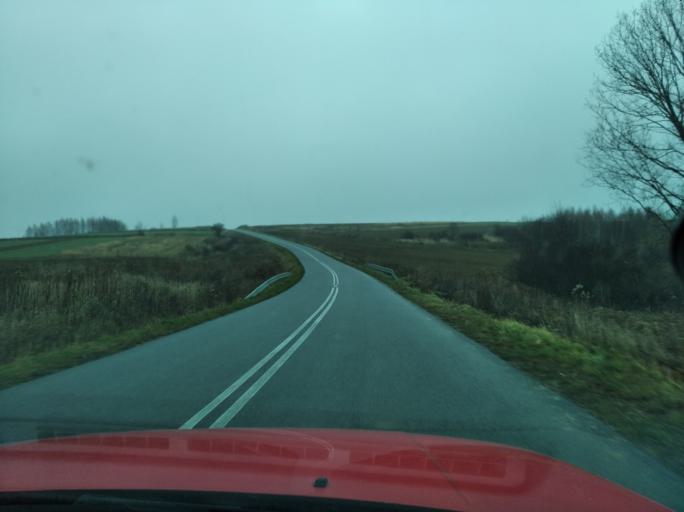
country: PL
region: Subcarpathian Voivodeship
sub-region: Powiat jaroslawski
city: Jodlowka
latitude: 49.8923
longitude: 22.4830
